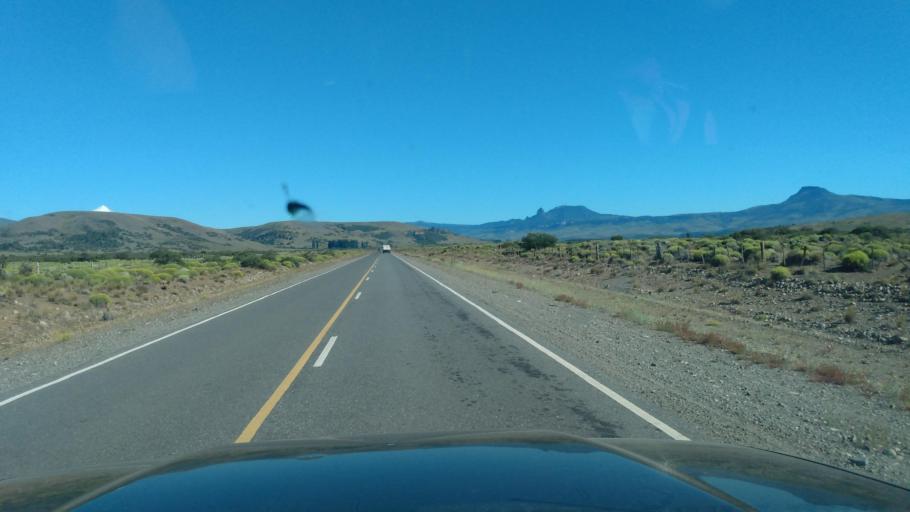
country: AR
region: Neuquen
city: Junin de los Andes
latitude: -39.8717
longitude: -71.1753
